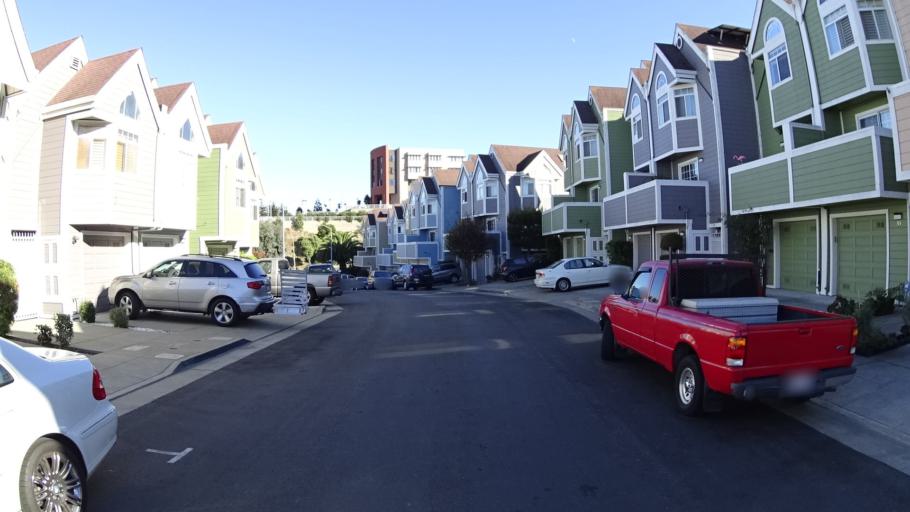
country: US
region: California
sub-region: San Francisco County
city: San Francisco
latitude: 37.7377
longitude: -122.3828
